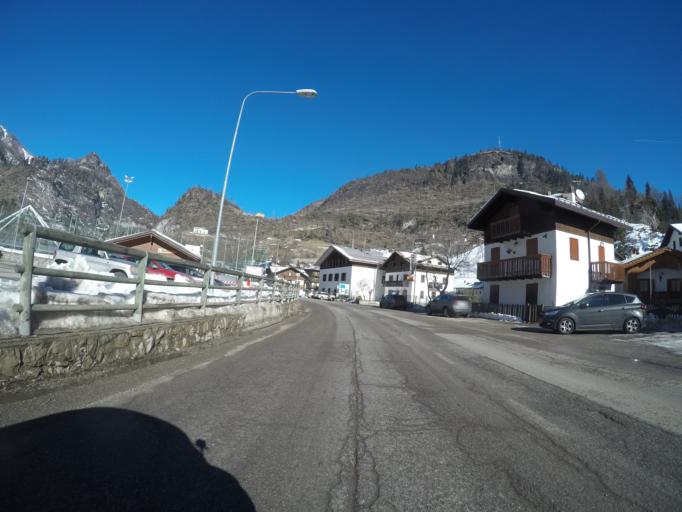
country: IT
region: Veneto
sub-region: Provincia di Belluno
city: Rocca Pietore
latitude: 46.4365
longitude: 11.9957
